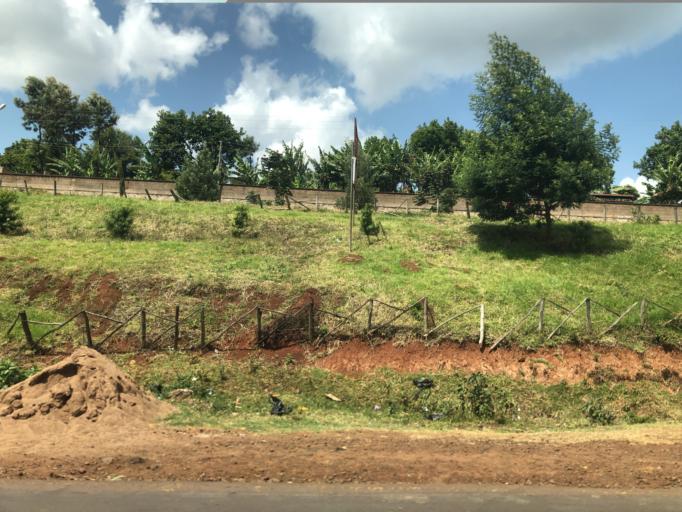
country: ET
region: Southern Nations, Nationalities, and People's Region
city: Boditi
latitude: 6.8718
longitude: 37.7694
